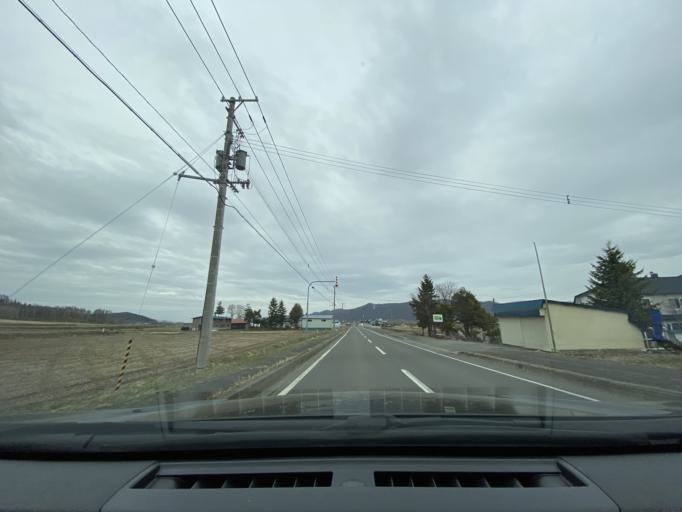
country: JP
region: Hokkaido
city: Nayoro
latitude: 44.1068
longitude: 142.4777
